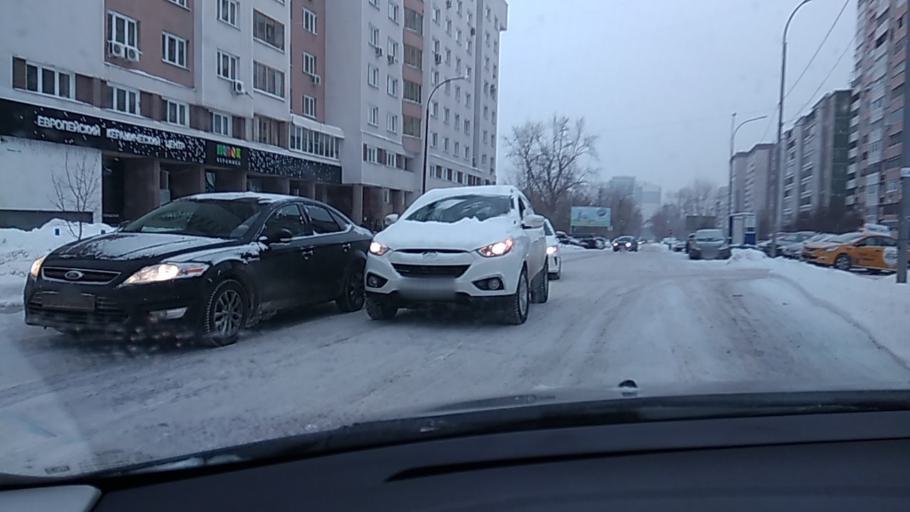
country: RU
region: Sverdlovsk
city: Yekaterinburg
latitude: 56.8076
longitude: 60.5987
